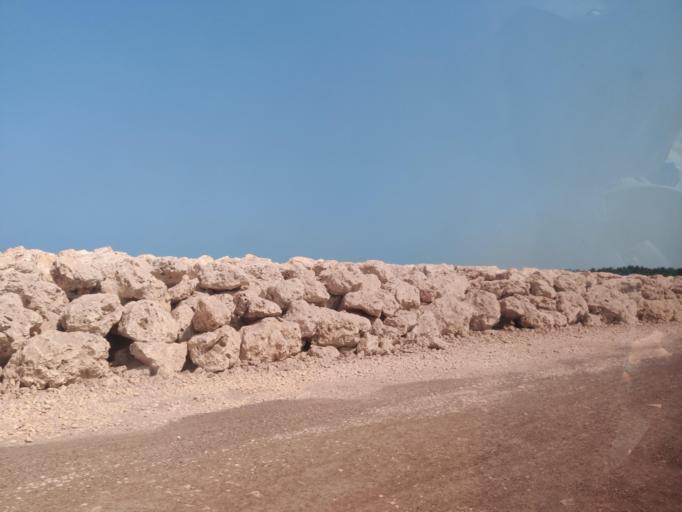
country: CO
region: Bolivar
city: Turbana
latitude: 10.1904
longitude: -75.6335
